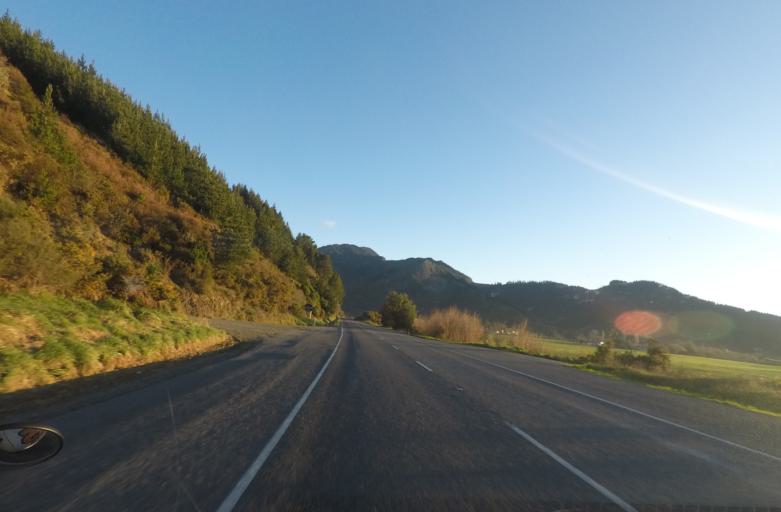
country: NZ
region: Marlborough
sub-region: Marlborough District
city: Picton
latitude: -41.2886
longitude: 173.6792
